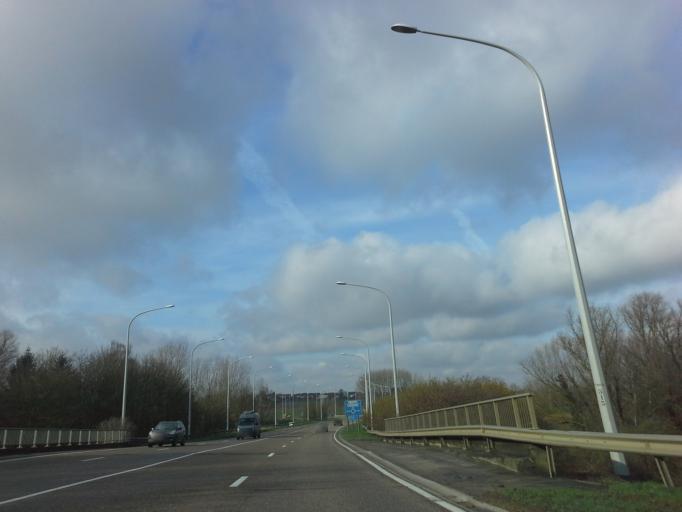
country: BE
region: Flanders
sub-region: Provincie Vlaams-Brabant
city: Tienen
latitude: 50.7926
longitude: 4.9346
